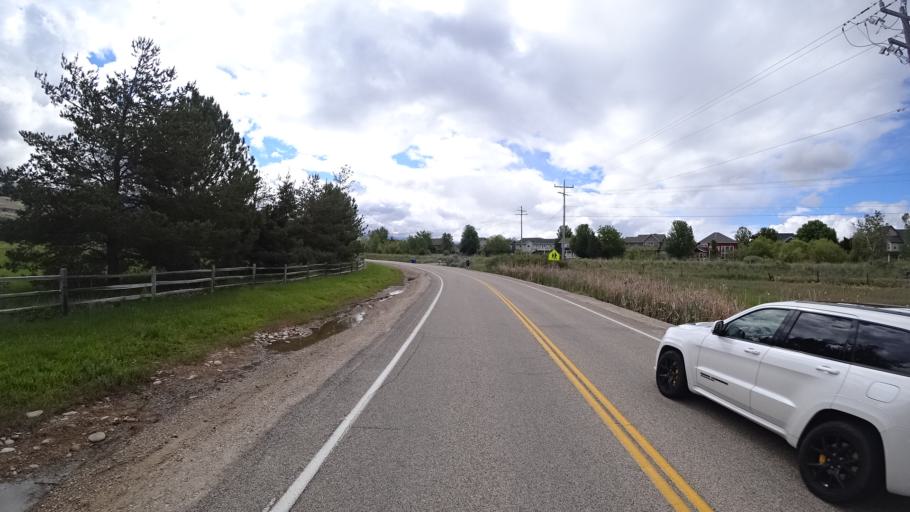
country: US
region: Idaho
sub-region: Ada County
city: Eagle
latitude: 43.7282
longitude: -116.2613
